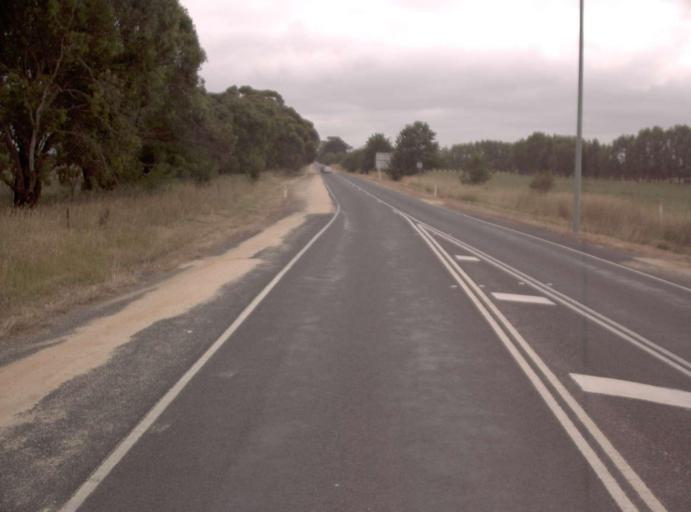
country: AU
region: Victoria
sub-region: Wellington
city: Heyfield
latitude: -38.0213
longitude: 146.7660
